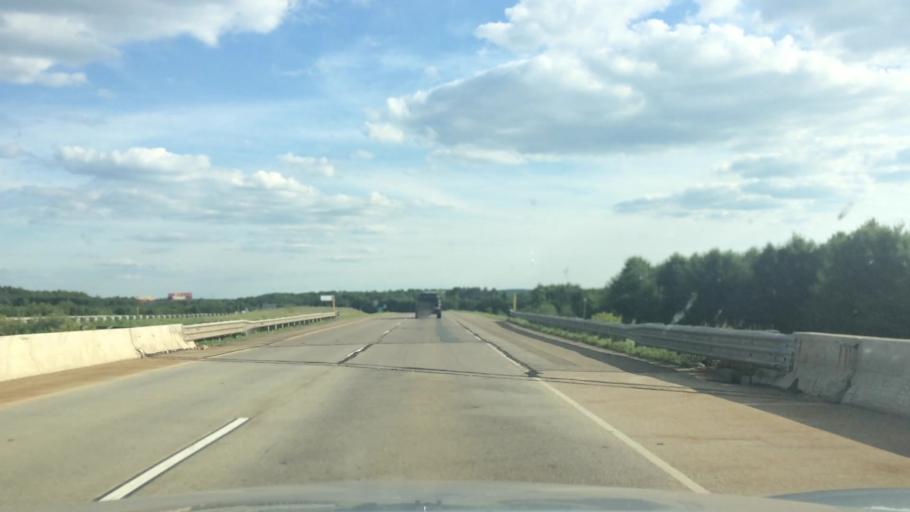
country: US
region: Wisconsin
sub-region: Lincoln County
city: Merrill
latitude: 45.1576
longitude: -89.6442
